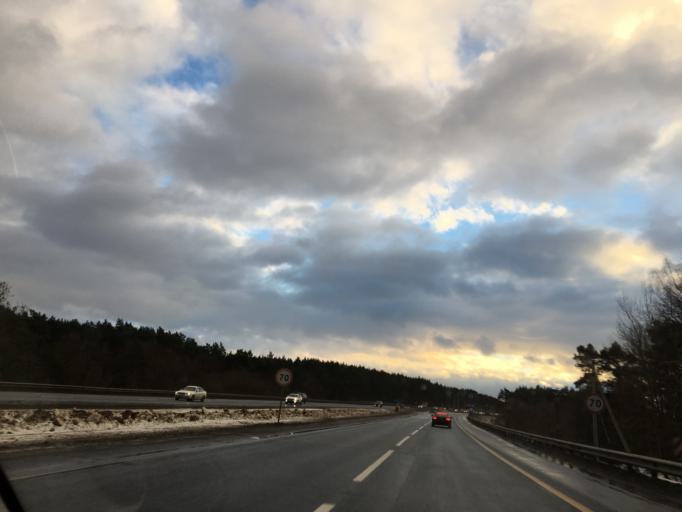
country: RU
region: Moskovskaya
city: Danki
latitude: 54.8876
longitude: 37.5117
